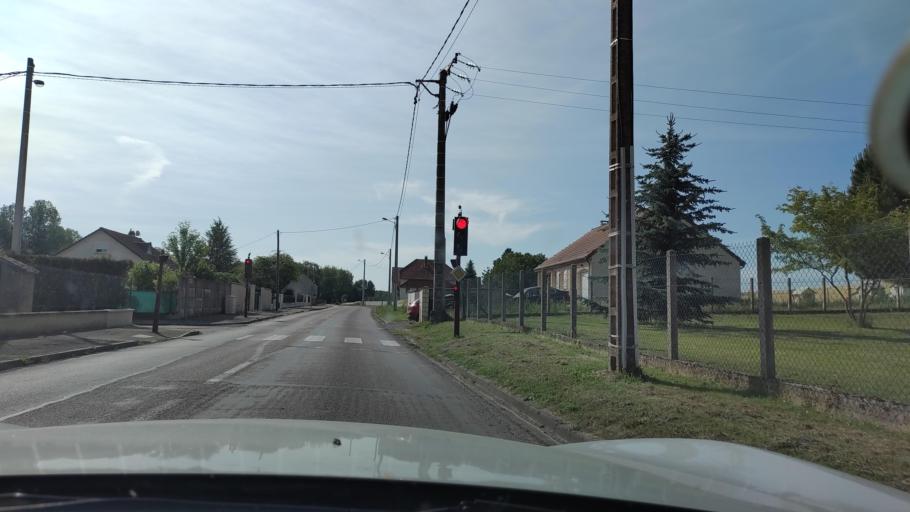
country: FR
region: Champagne-Ardenne
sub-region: Departement de l'Aube
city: Nogent-sur-Seine
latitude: 48.4727
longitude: 3.5592
